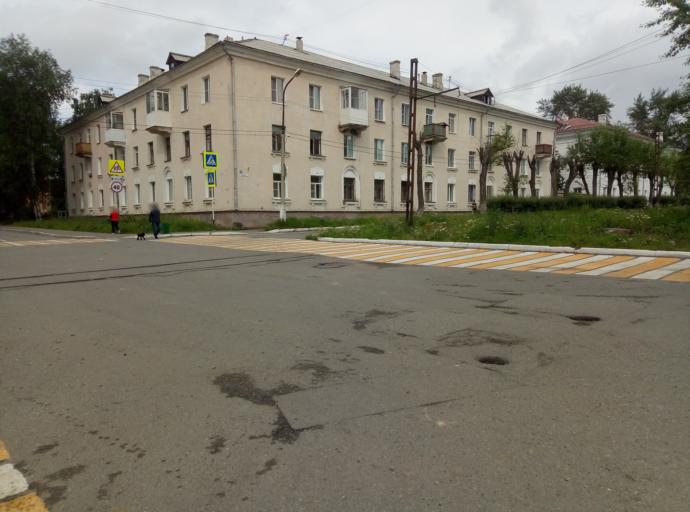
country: RU
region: Sverdlovsk
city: Krasnotur'insk
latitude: 59.7619
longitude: 60.1875
